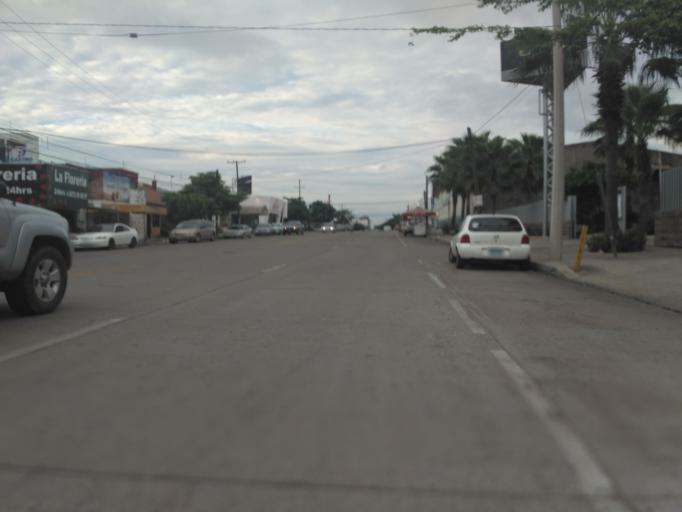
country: MX
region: Sinaloa
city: Culiacan
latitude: 24.7967
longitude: -107.4044
